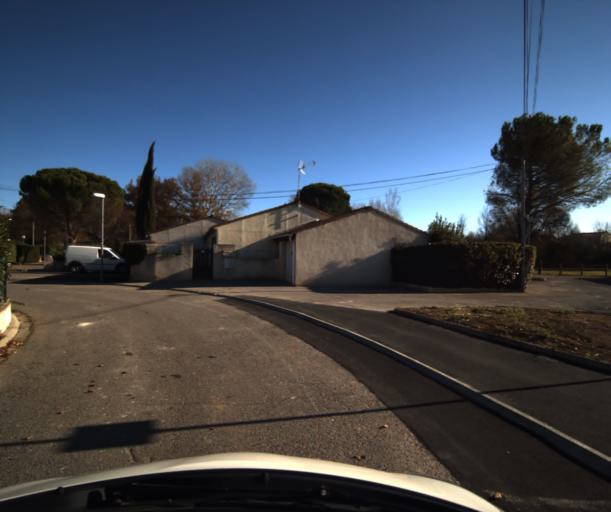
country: FR
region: Provence-Alpes-Cote d'Azur
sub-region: Departement du Vaucluse
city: Pertuis
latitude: 43.6998
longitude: 5.5094
